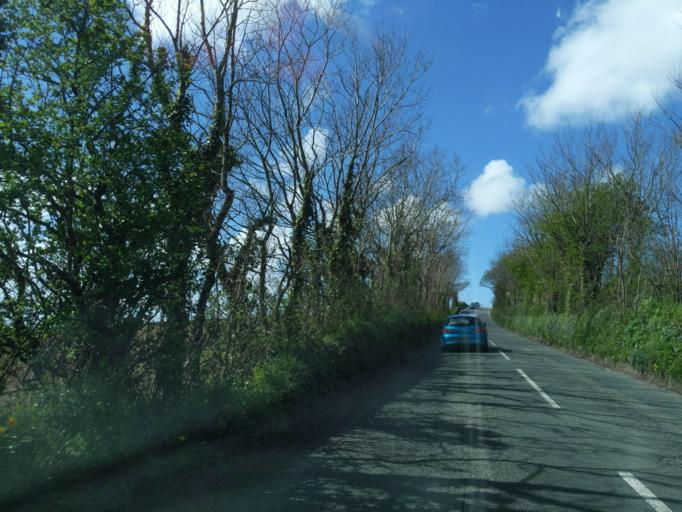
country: GB
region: England
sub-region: Cornwall
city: Wadebridge
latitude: 50.5344
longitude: -4.8461
